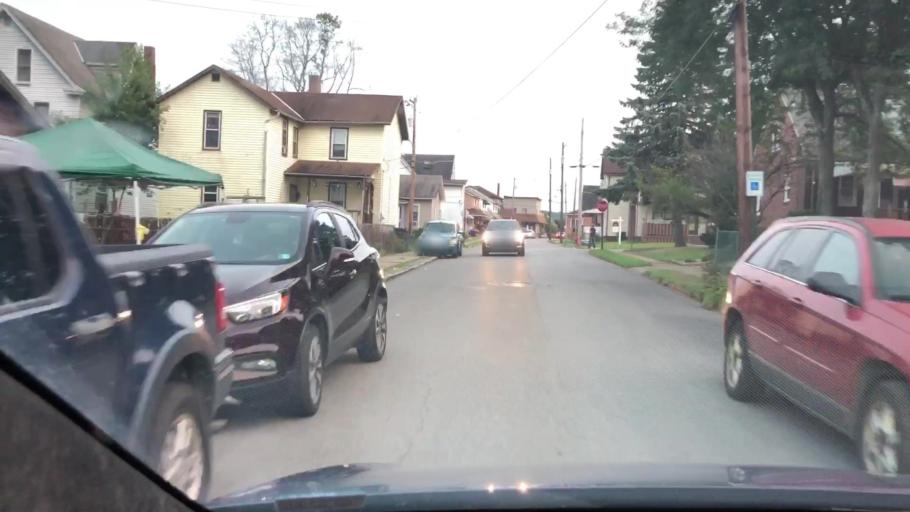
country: US
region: Pennsylvania
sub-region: Butler County
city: Butler
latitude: 40.8644
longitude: -79.9086
